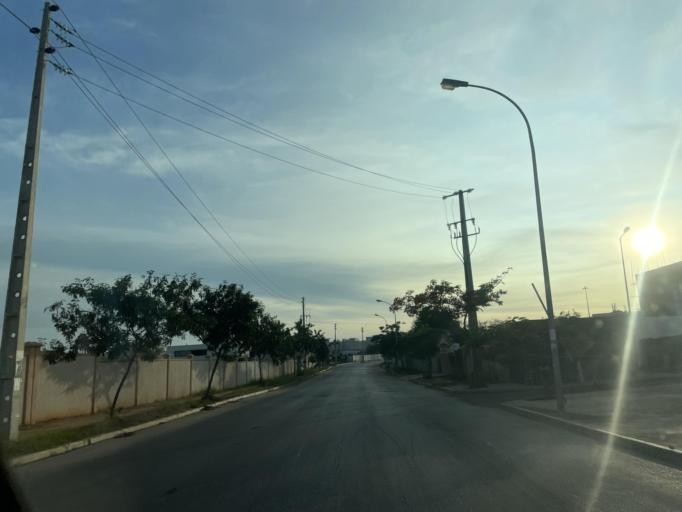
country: AO
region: Luanda
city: Luanda
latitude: -8.9296
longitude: 13.1912
